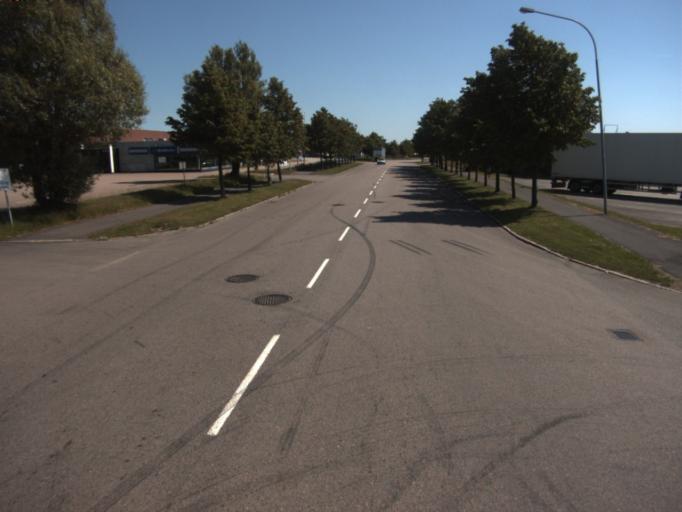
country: SE
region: Skane
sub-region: Helsingborg
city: Gantofta
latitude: 56.0064
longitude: 12.7700
